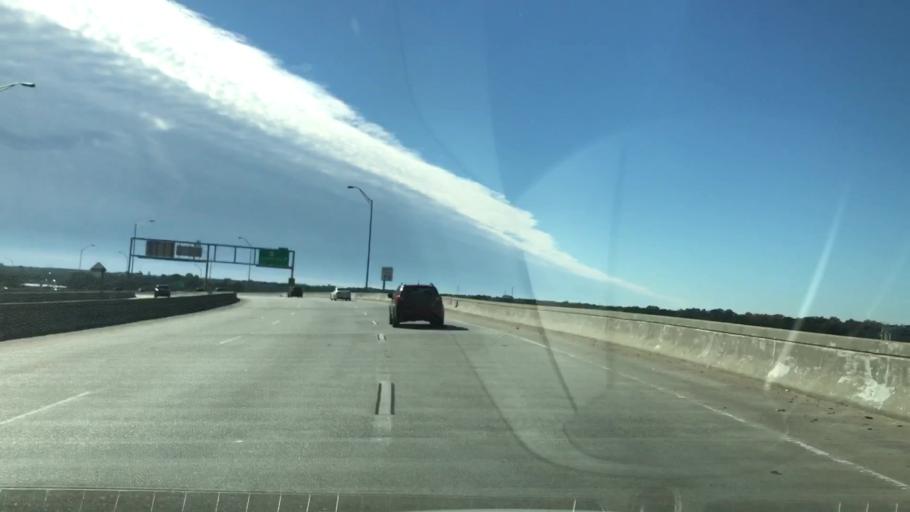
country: US
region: South Carolina
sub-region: Charleston County
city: Charleston
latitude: 32.7798
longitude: -79.9569
